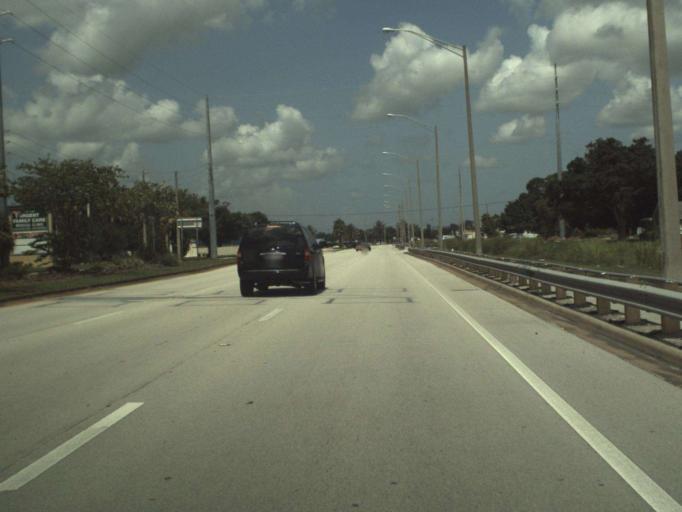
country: US
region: Florida
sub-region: Saint Lucie County
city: Fort Pierce South
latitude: 27.4256
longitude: -80.3630
